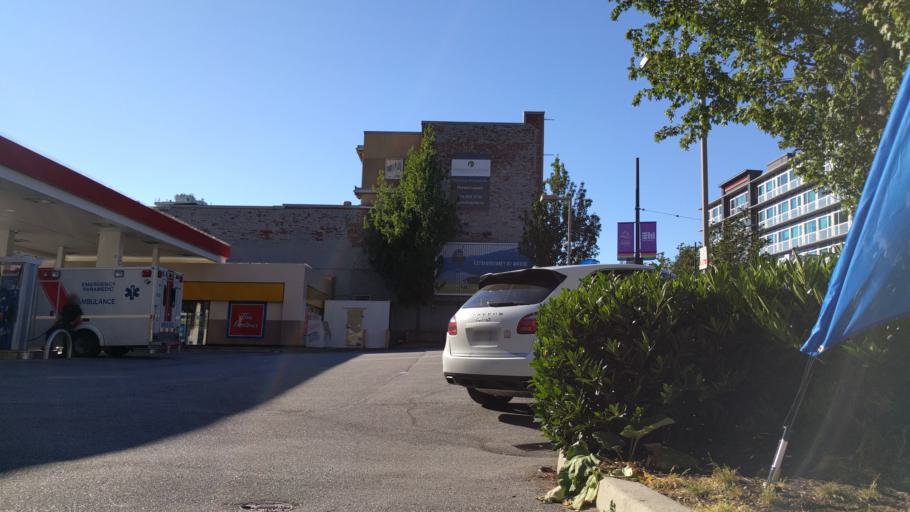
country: CA
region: British Columbia
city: West End
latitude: 49.2791
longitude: -123.1292
